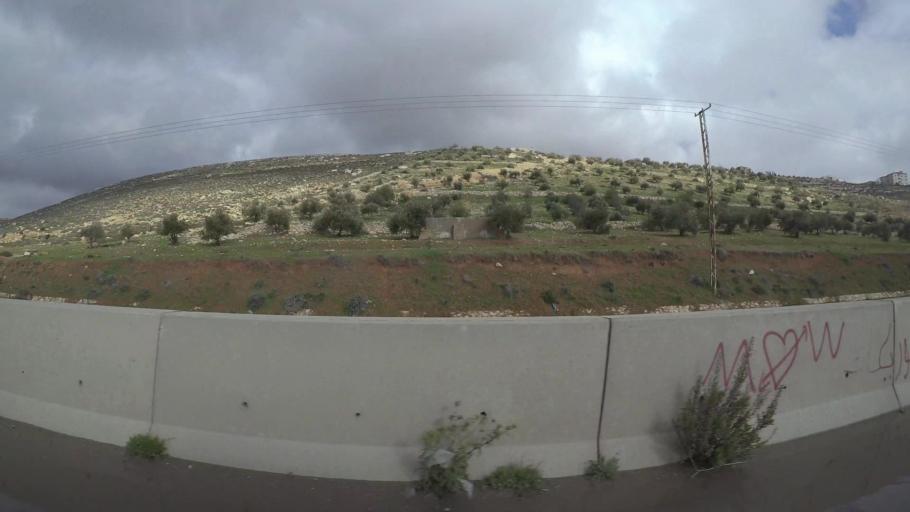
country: JO
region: Amman
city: Al Jubayhah
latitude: 32.0772
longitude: 35.8786
